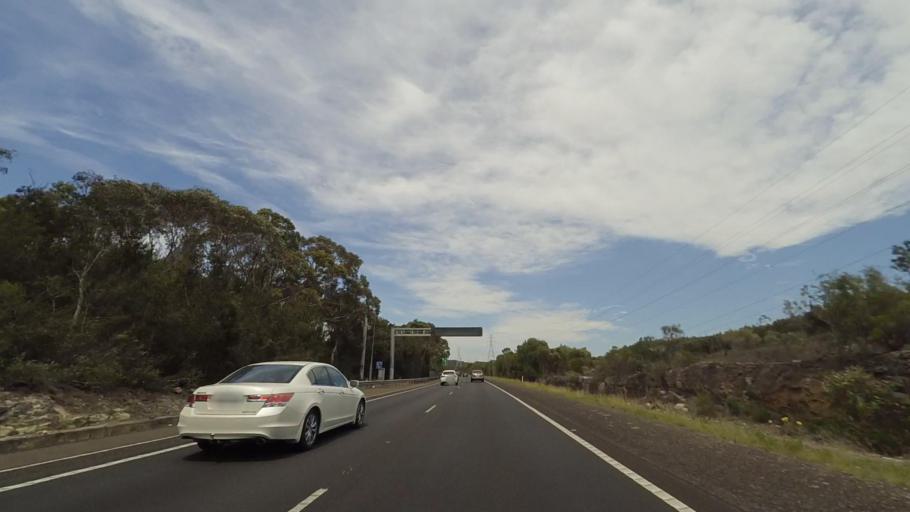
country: AU
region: New South Wales
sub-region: Wollongong
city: Helensburgh
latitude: -34.1885
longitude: 150.9683
